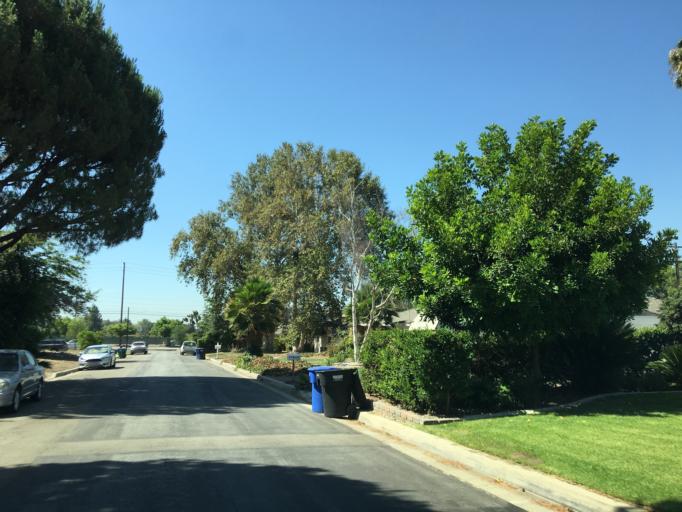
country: US
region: California
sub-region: Los Angeles County
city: Claremont
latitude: 34.1229
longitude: -117.7344
